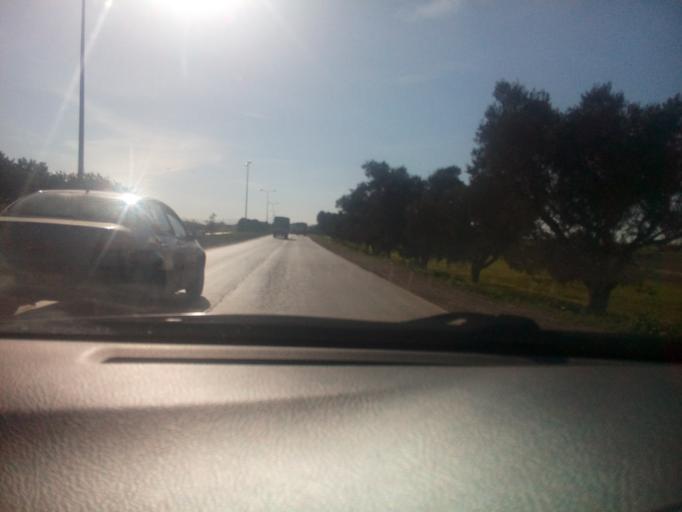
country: DZ
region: Oran
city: Sidi ech Chahmi
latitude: 35.6667
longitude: -0.5669
